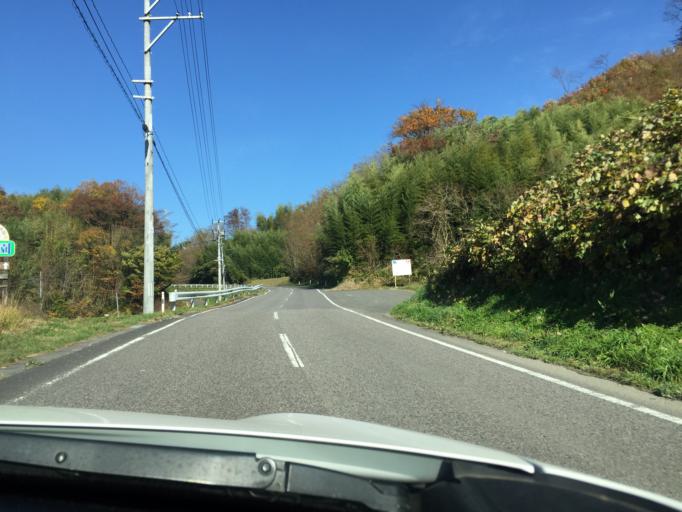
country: JP
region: Fukushima
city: Miharu
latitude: 37.4060
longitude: 140.4719
